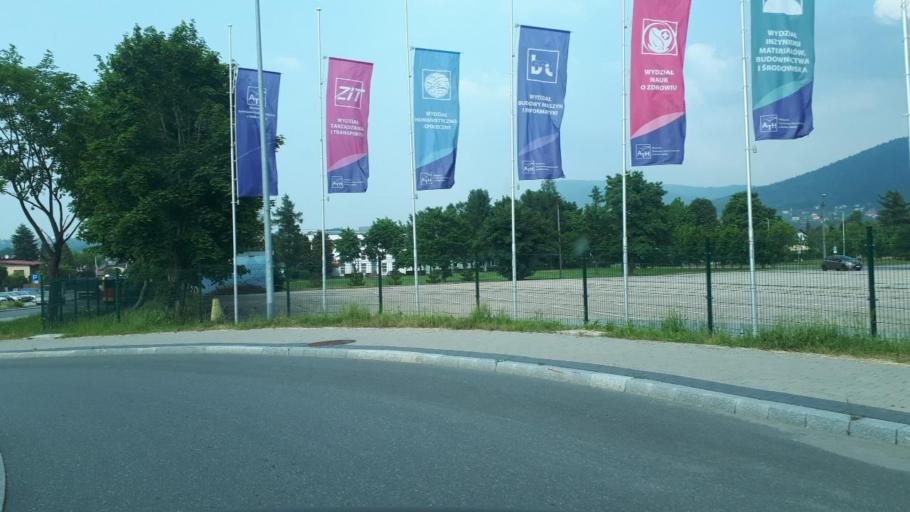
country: PL
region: Silesian Voivodeship
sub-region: Powiat bielski
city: Bystra
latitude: 49.7837
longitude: 19.0559
